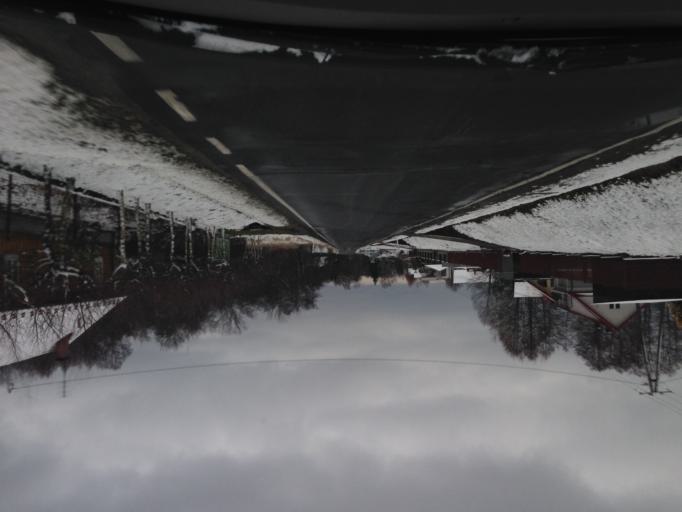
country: PL
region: Lesser Poland Voivodeship
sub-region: Powiat brzeski
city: Iwkowa
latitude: 49.8510
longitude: 20.5993
